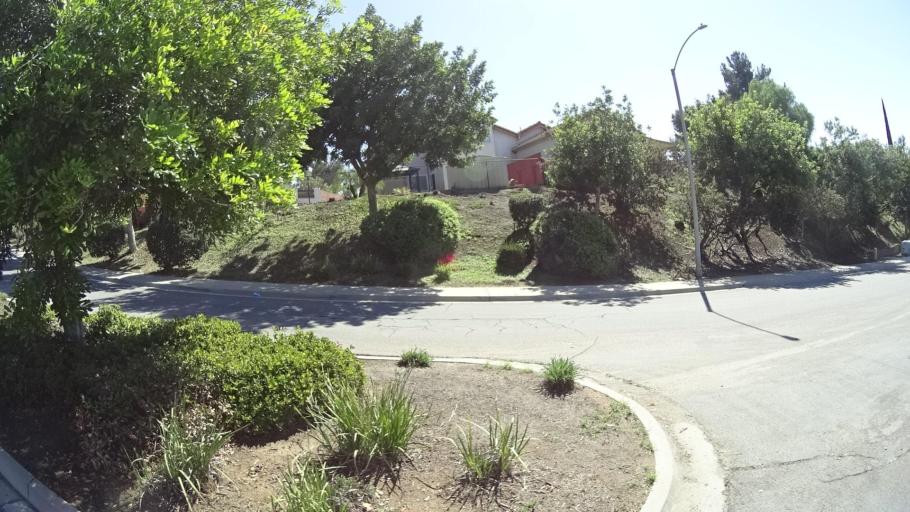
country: US
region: California
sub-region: San Diego County
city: Rancho San Diego
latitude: 32.7505
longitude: -116.9261
